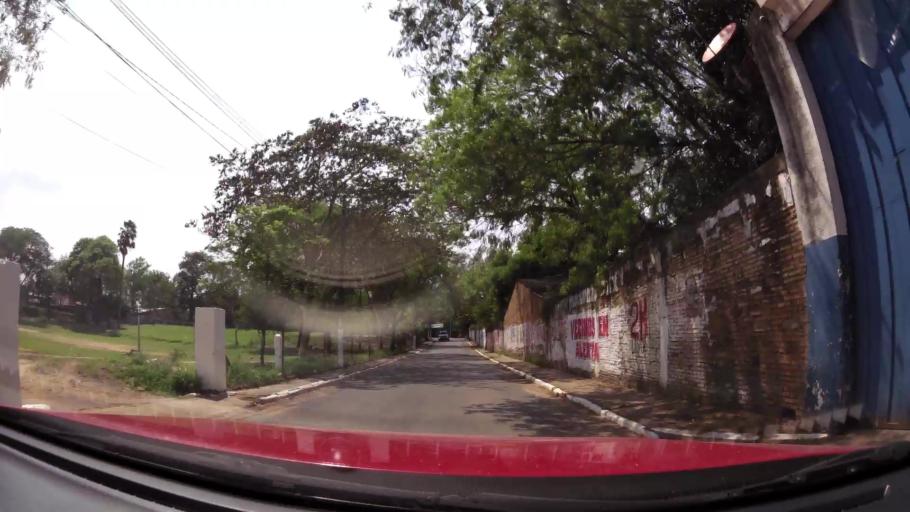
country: PY
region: Asuncion
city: Asuncion
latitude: -25.2799
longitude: -57.5877
